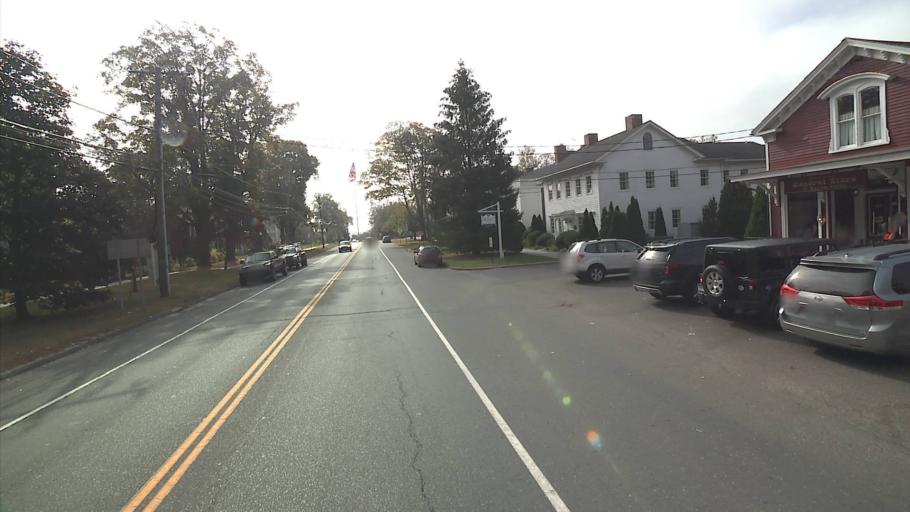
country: US
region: Connecticut
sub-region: Fairfield County
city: Newtown
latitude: 41.4149
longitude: -73.3098
